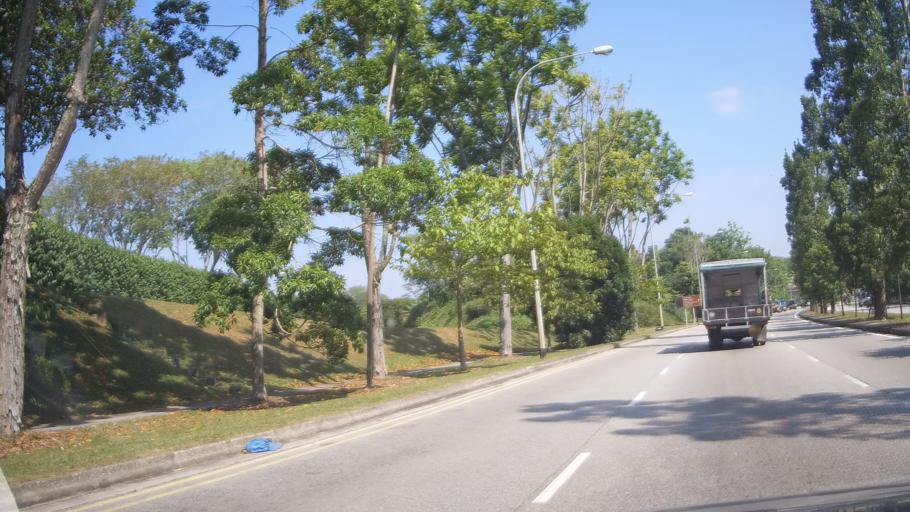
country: MY
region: Johor
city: Johor Bahru
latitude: 1.4194
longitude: 103.7590
